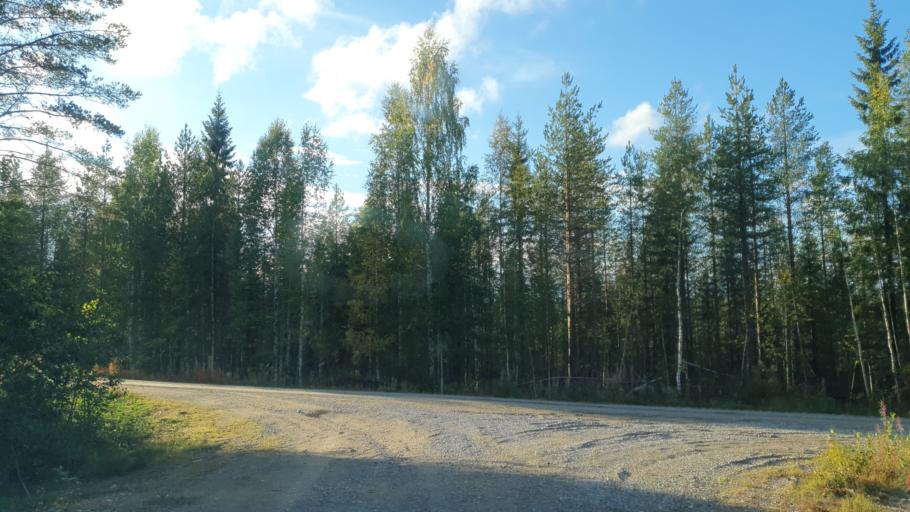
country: FI
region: Kainuu
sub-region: Kehys-Kainuu
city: Kuhmo
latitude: 64.3402
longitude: 29.9781
